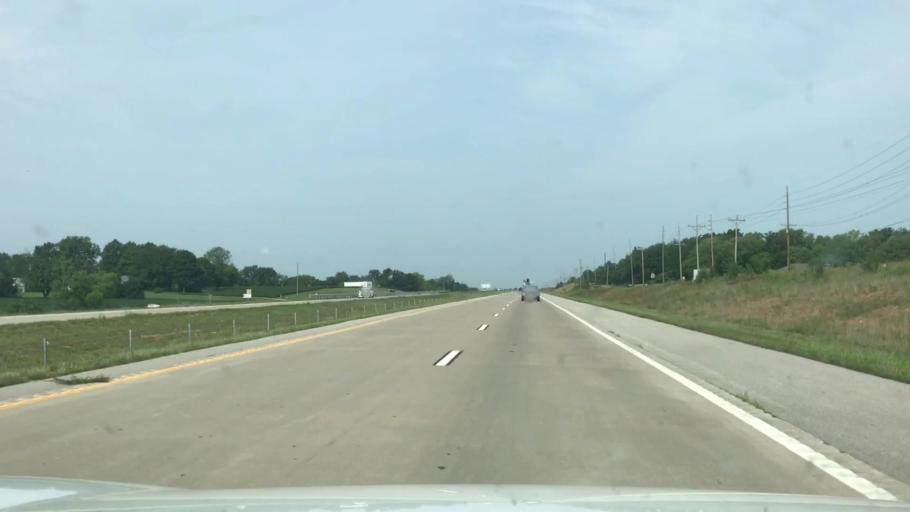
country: US
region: Missouri
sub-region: Saint Charles County
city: Dardenne Prairie
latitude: 38.7614
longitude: -90.7200
